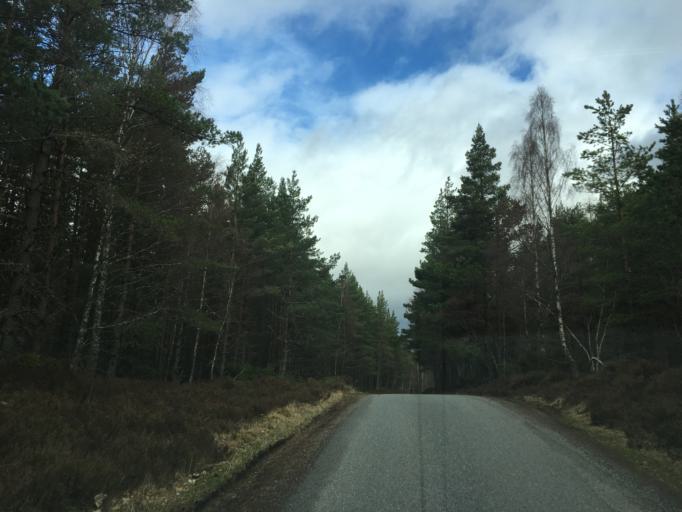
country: GB
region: Scotland
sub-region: Highland
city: Kingussie
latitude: 57.1015
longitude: -3.9214
